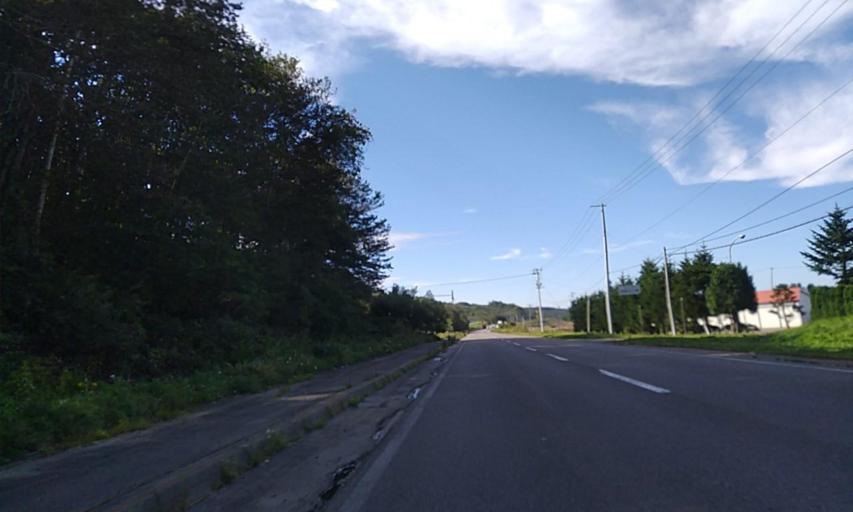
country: JP
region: Hokkaido
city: Obihiro
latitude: 42.8189
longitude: 143.4837
